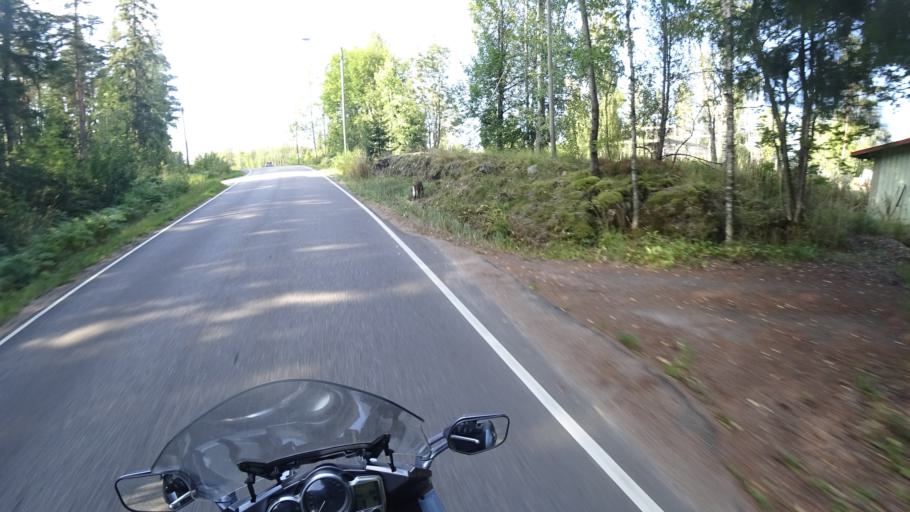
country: FI
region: Varsinais-Suomi
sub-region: Salo
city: Suomusjaervi
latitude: 60.3699
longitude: 23.6447
